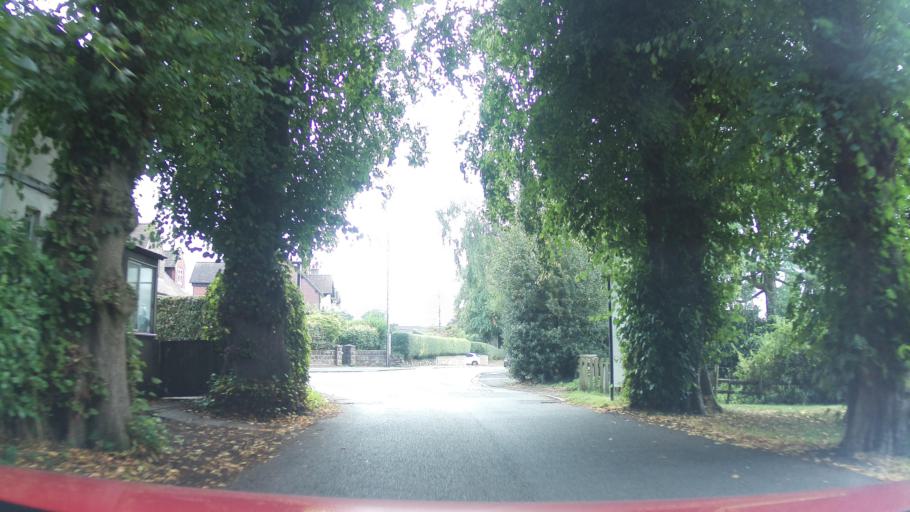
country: GB
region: England
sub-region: Staffordshire
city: Barlaston
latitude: 52.9470
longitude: -2.1578
